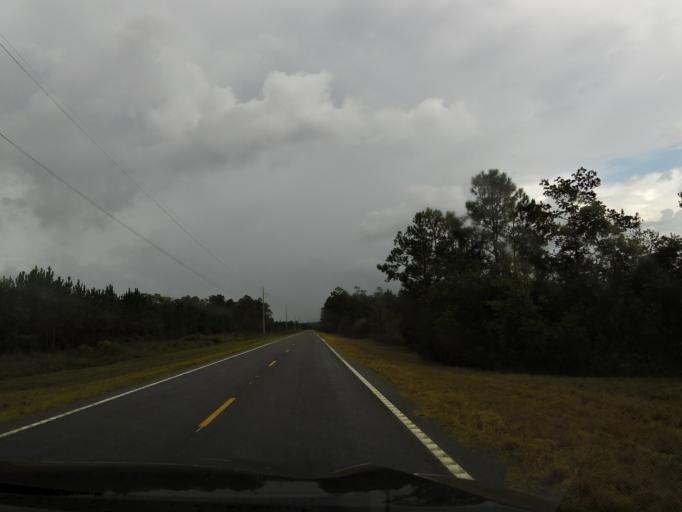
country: US
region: Florida
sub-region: Duval County
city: Baldwin
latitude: 30.4783
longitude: -82.0480
